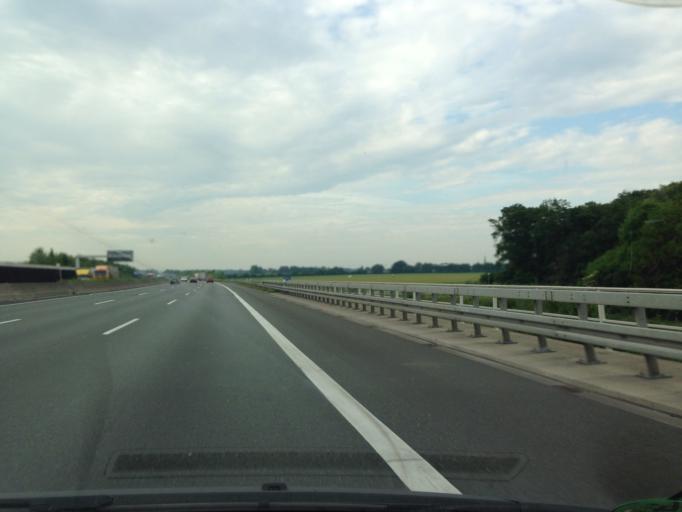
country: DE
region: North Rhine-Westphalia
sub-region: Regierungsbezirk Munster
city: Muenster
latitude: 51.9683
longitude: 7.5467
